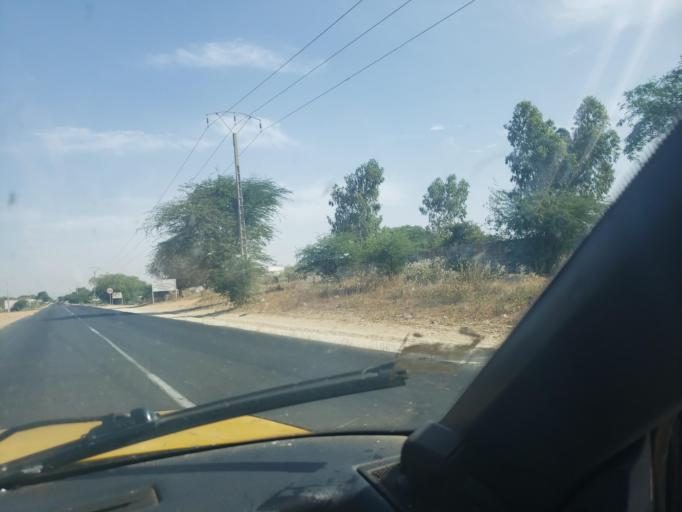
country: SN
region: Saint-Louis
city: Saint-Louis
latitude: 15.9304
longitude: -16.3294
